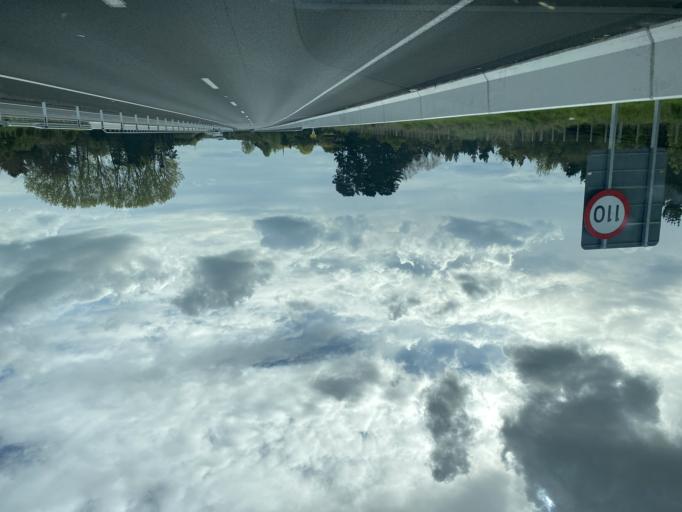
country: NZ
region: Waikato
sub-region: Waipa District
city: Cambridge
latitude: -37.8898
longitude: 175.4973
